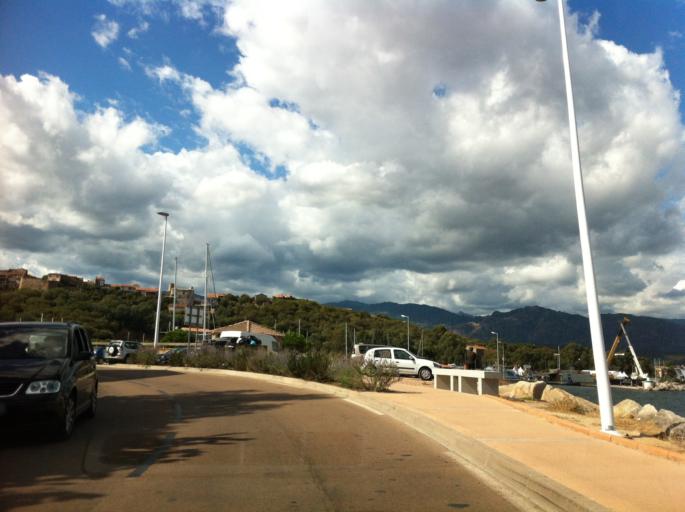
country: FR
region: Corsica
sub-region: Departement de la Corse-du-Sud
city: Porto-Vecchio
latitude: 41.5889
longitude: 9.2866
